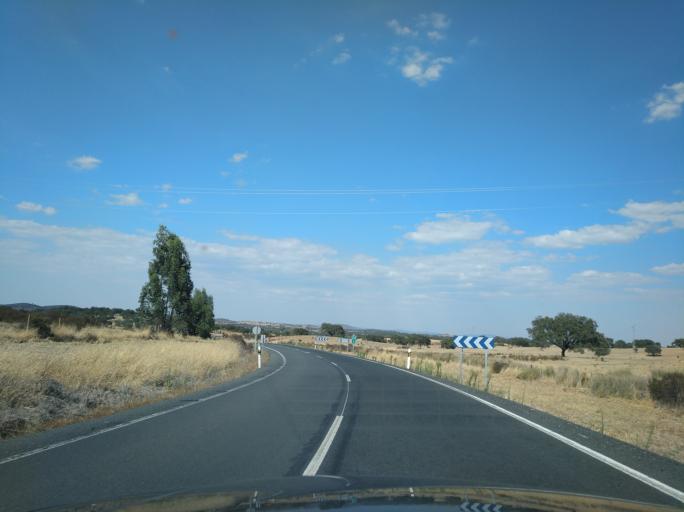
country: ES
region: Andalusia
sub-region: Provincia de Huelva
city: Cabezas Rubias
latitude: 37.6439
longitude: -7.1260
